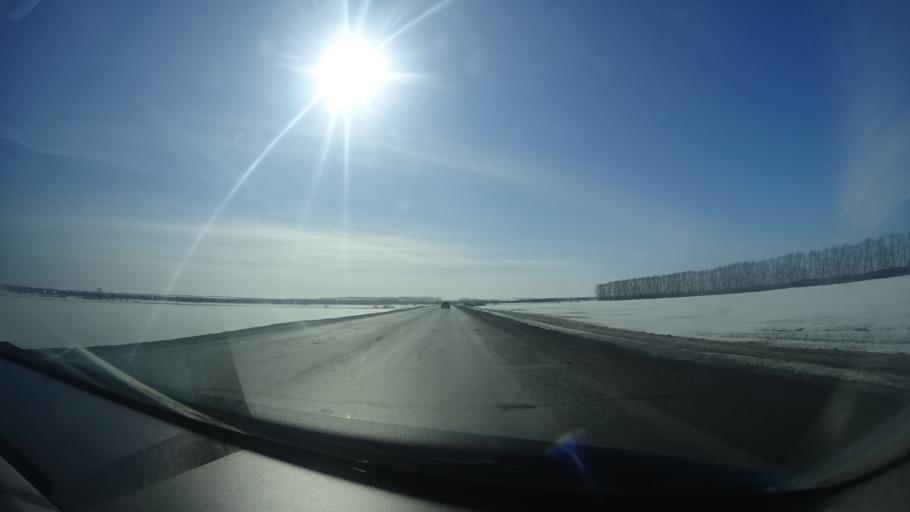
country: RU
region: Bashkortostan
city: Mikhaylovka
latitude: 54.9359
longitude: 55.7448
